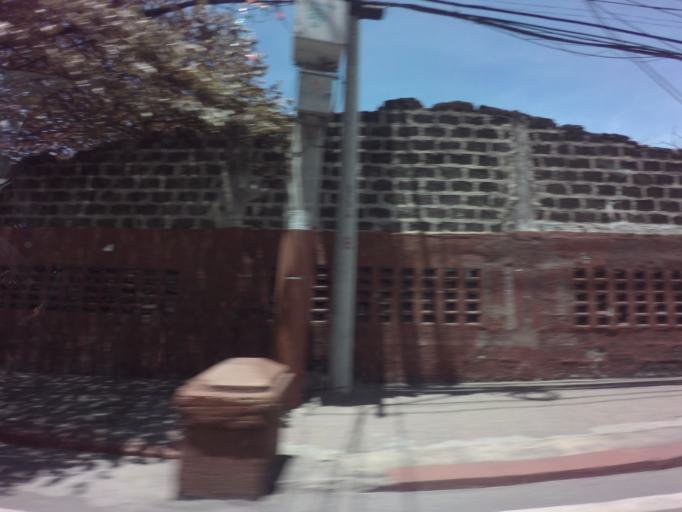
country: PH
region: Calabarzon
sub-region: Province of Rizal
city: Las Pinas
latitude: 14.4750
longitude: 120.9783
